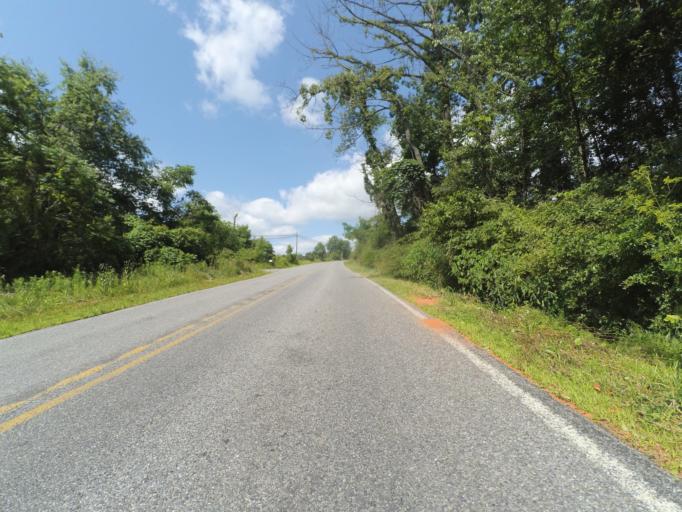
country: US
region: Pennsylvania
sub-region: Centre County
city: Stormstown
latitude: 40.7839
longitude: -78.0494
